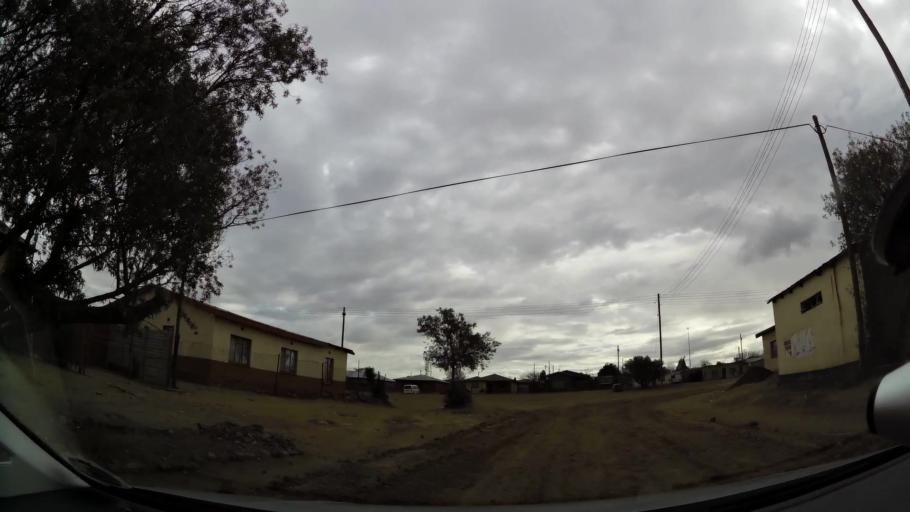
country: ZA
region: Orange Free State
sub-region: Fezile Dabi District Municipality
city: Kroonstad
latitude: -27.6503
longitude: 27.2077
